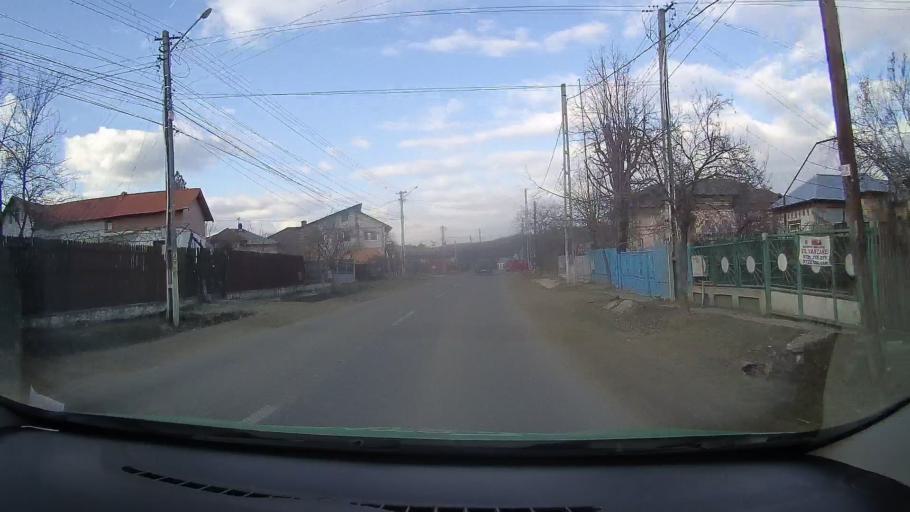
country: RO
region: Dambovita
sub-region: Comuna Gura Ocnitei
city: Gura Ocnitei
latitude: 44.9353
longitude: 25.5620
